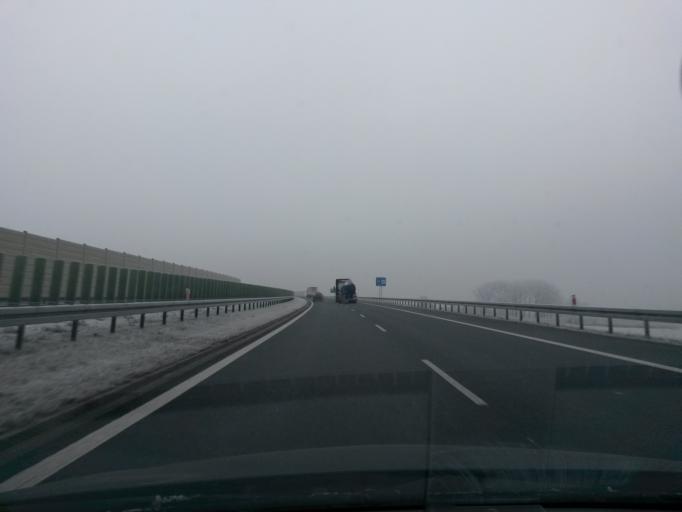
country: PL
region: Greater Poland Voivodeship
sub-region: Powiat gnieznienski
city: Lubowo
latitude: 52.5002
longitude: 17.4619
